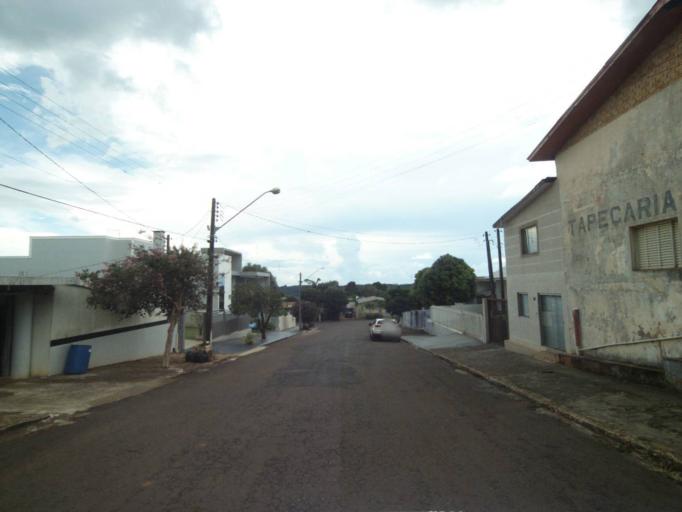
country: BR
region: Parana
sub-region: Guaraniacu
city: Guaraniacu
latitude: -25.0975
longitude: -52.8712
